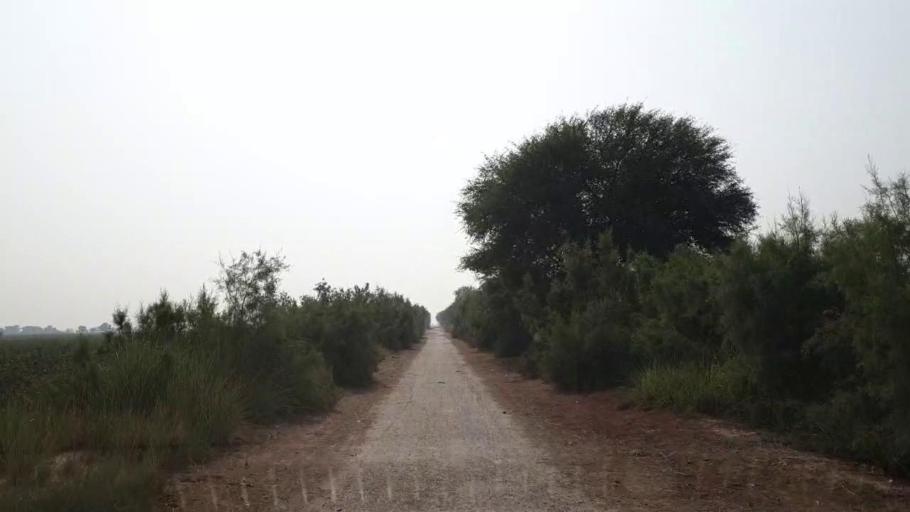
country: PK
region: Sindh
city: Bhan
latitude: 26.4675
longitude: 67.7390
